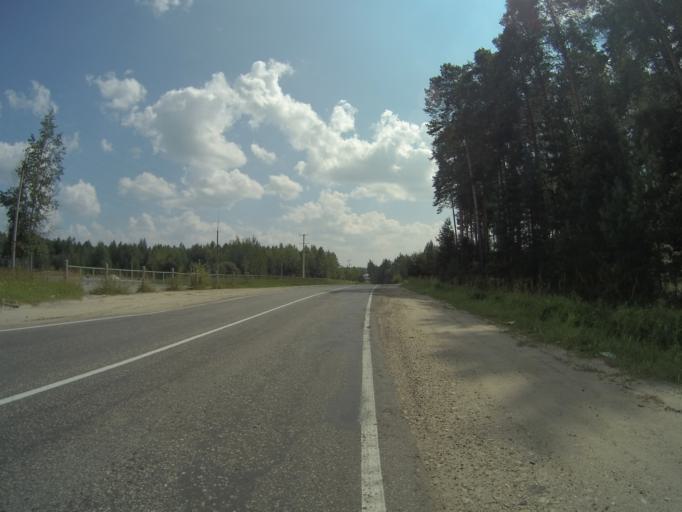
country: RU
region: Vladimir
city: Gus'-Khrustal'nyy
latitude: 55.6394
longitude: 40.7084
